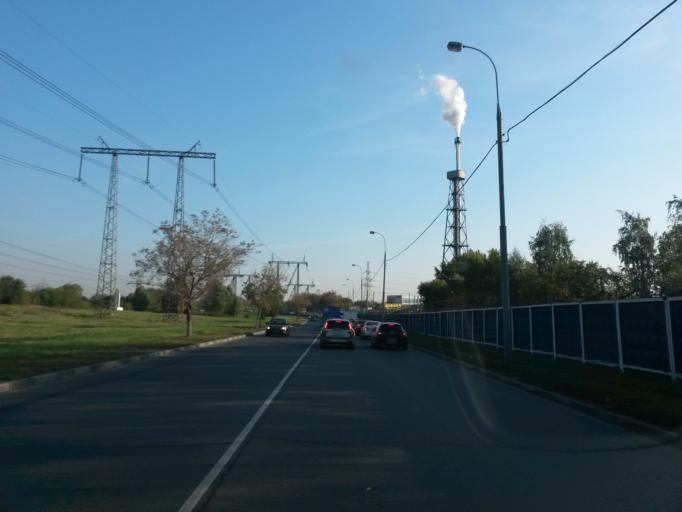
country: RU
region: Moscow
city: Kapotnya
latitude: 55.6550
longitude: 37.7943
